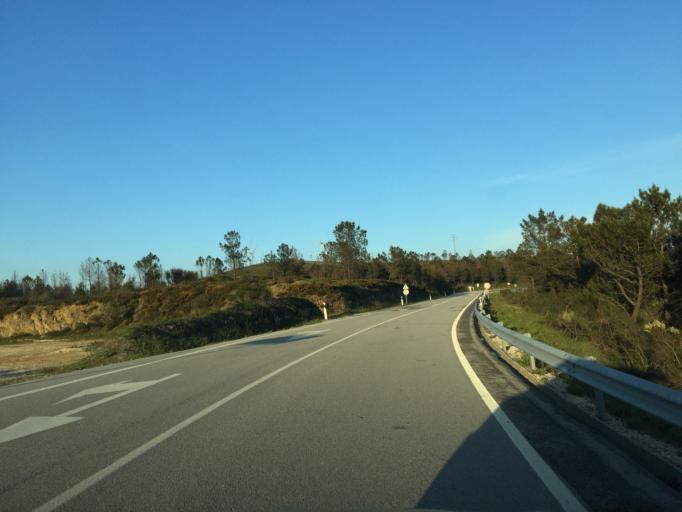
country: PT
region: Coimbra
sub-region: Gois
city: Gois
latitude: 40.1106
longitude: -8.0308
